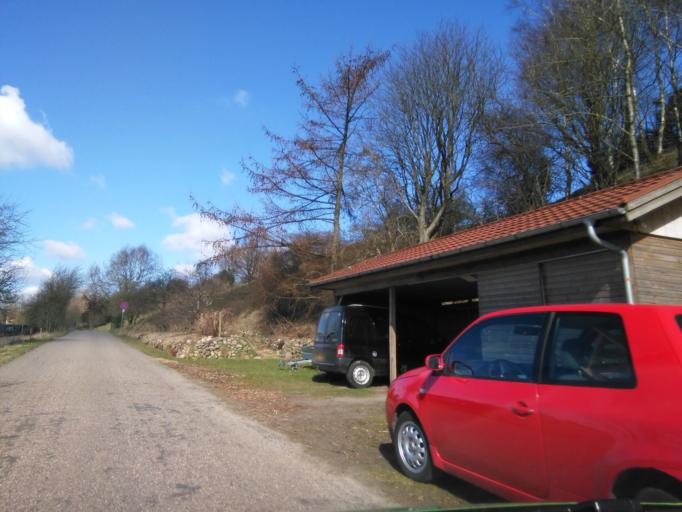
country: DK
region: Central Jutland
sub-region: Skanderborg Kommune
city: Ry
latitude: 56.1077
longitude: 9.7378
